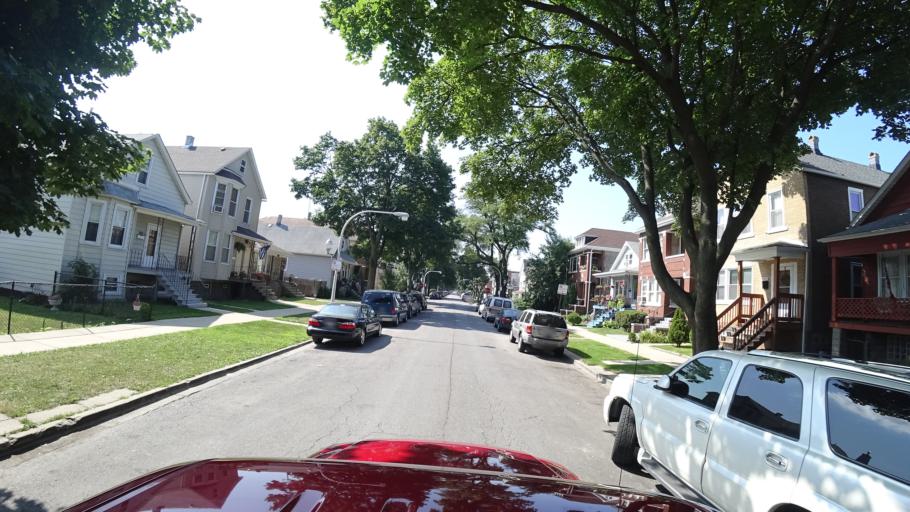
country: US
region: Illinois
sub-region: Cook County
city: Chicago
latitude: 41.8217
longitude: -87.6861
